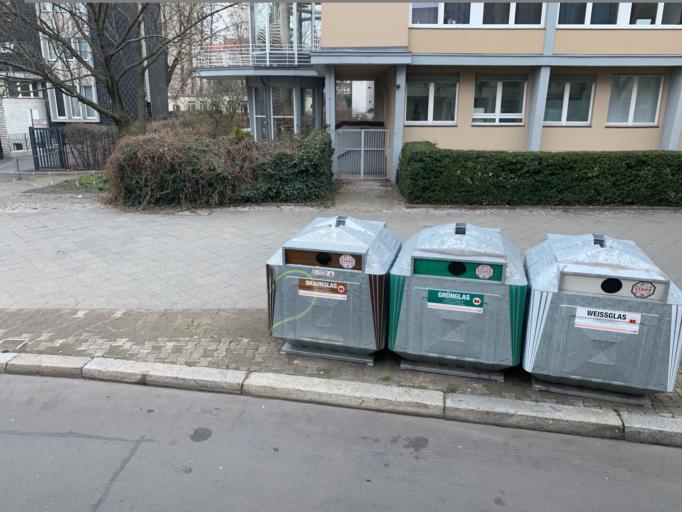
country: DE
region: Berlin
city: Charlottenburg Bezirk
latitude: 52.5073
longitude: 13.2954
